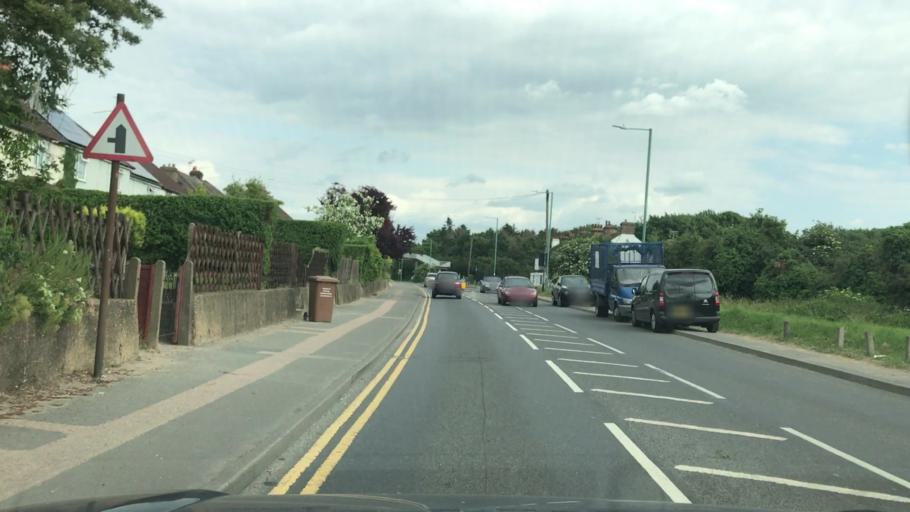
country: GB
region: England
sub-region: Kent
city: Stone
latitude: 51.4174
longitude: 0.2579
